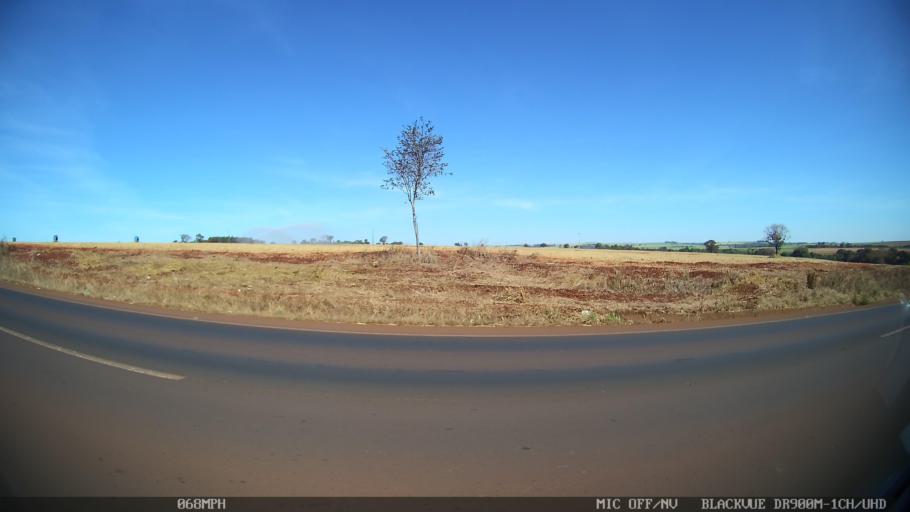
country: BR
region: Sao Paulo
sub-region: Sao Joaquim Da Barra
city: Sao Joaquim da Barra
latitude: -20.5173
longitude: -47.8789
